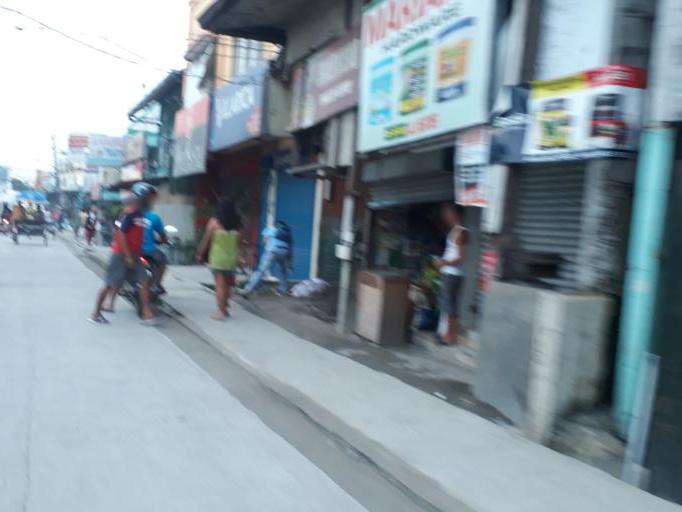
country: PH
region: Central Luzon
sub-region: Province of Bulacan
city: Obando
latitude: 14.7083
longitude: 120.9465
